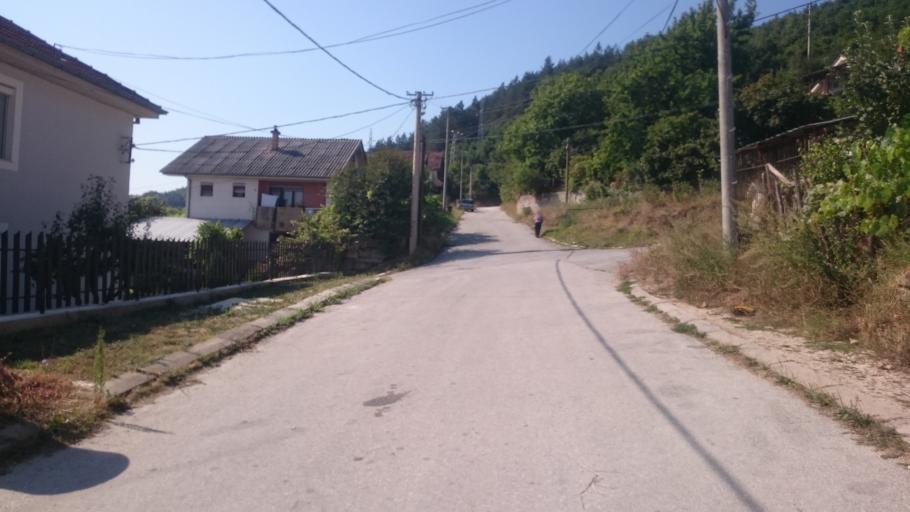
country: MK
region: Makedonski Brod
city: Makedonski Brod
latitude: 41.5115
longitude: 21.2138
